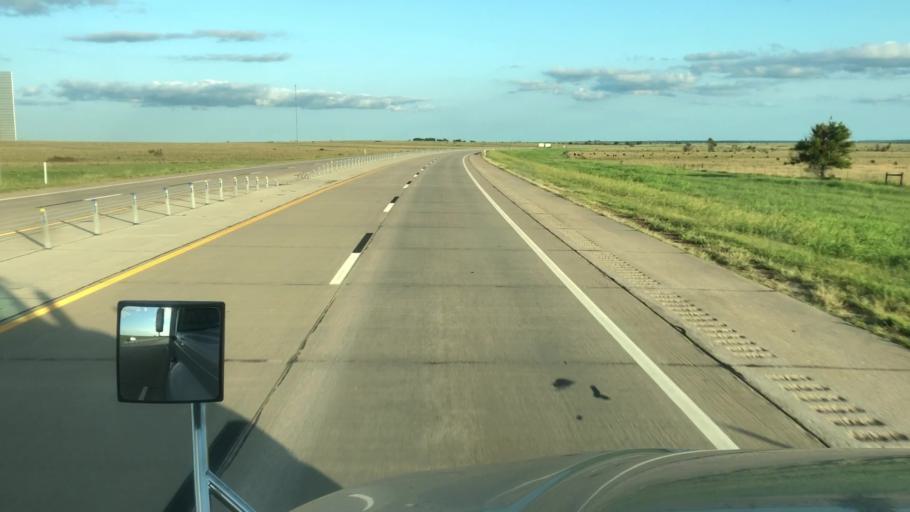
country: US
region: Oklahoma
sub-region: Pawnee County
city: Pawnee
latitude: 36.3751
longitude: -97.0416
